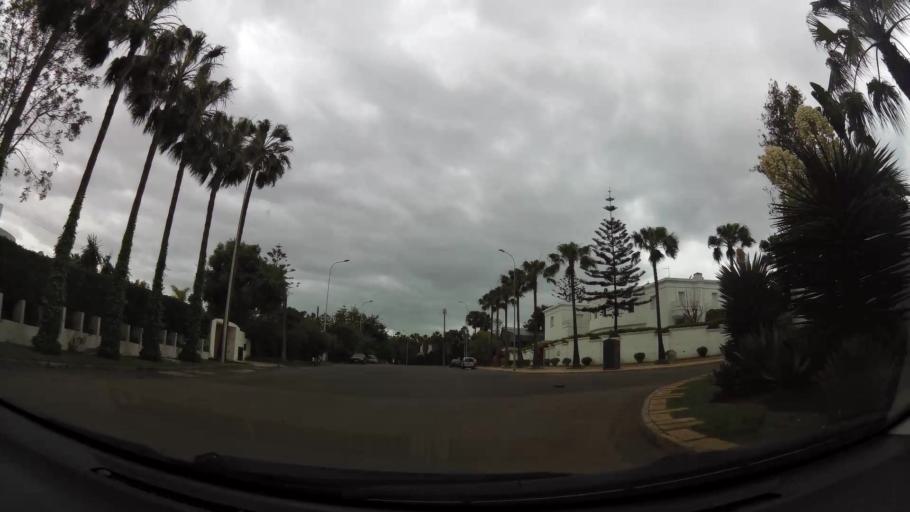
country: MA
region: Grand Casablanca
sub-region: Casablanca
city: Casablanca
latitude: 33.5815
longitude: -7.6688
